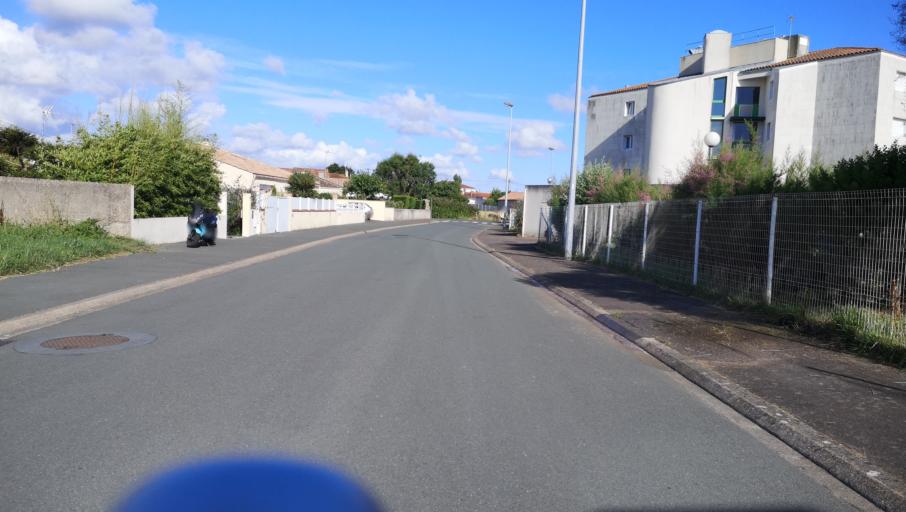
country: FR
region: Pays de la Loire
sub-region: Departement de la Vendee
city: Les Sables-d'Olonne
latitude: 46.5089
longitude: -1.7880
